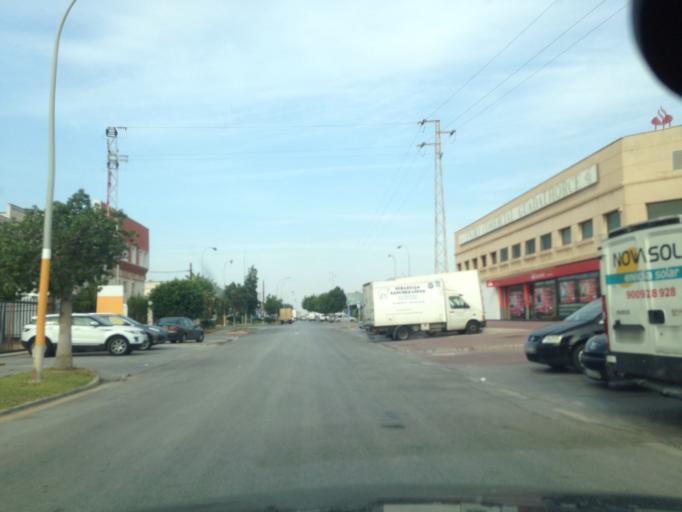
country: ES
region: Andalusia
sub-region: Provincia de Malaga
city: Malaga
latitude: 36.6885
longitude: -4.4717
